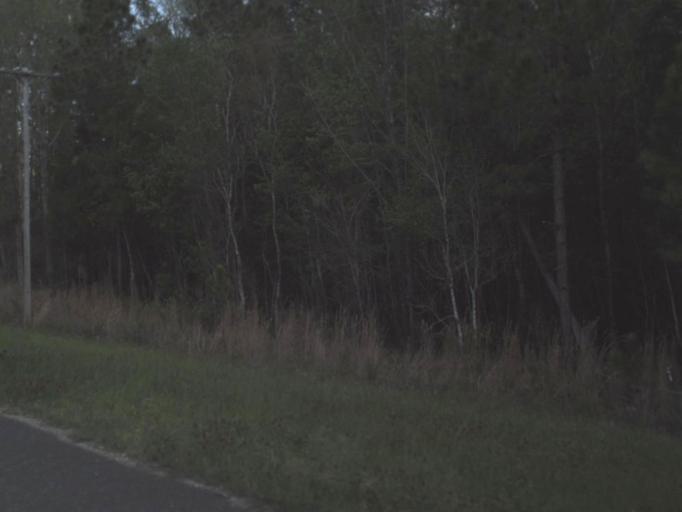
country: US
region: Florida
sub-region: Santa Rosa County
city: Point Baker
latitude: 30.8837
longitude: -86.9614
